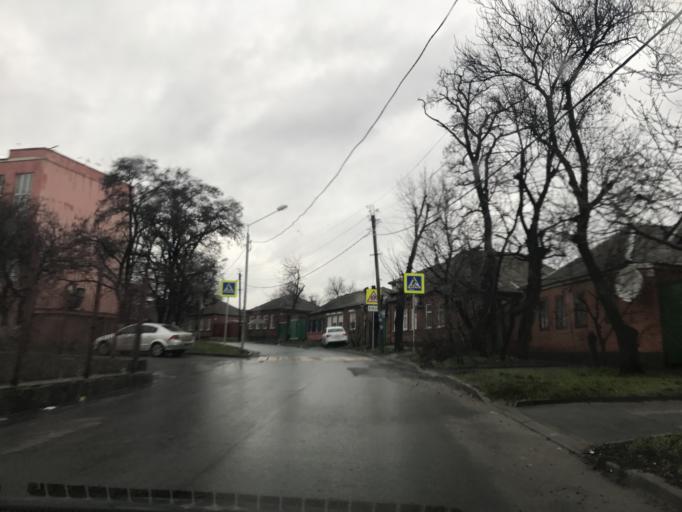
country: RU
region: Rostov
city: Rostov-na-Donu
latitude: 47.2321
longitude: 39.6795
